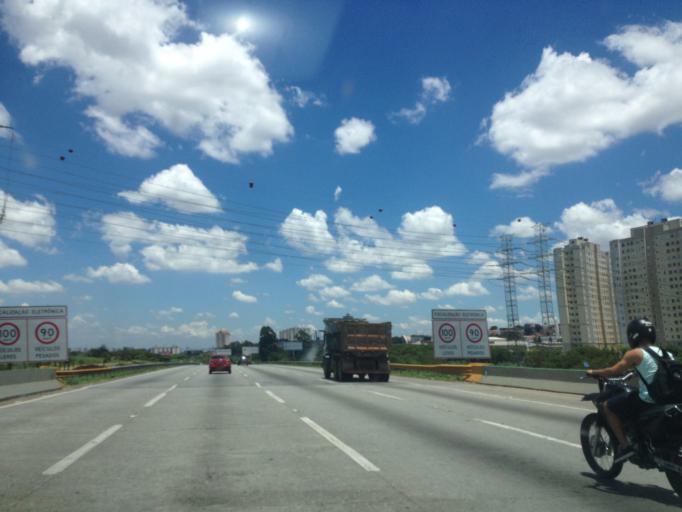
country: BR
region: Sao Paulo
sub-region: Guarulhos
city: Guarulhos
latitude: -23.4932
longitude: -46.5391
